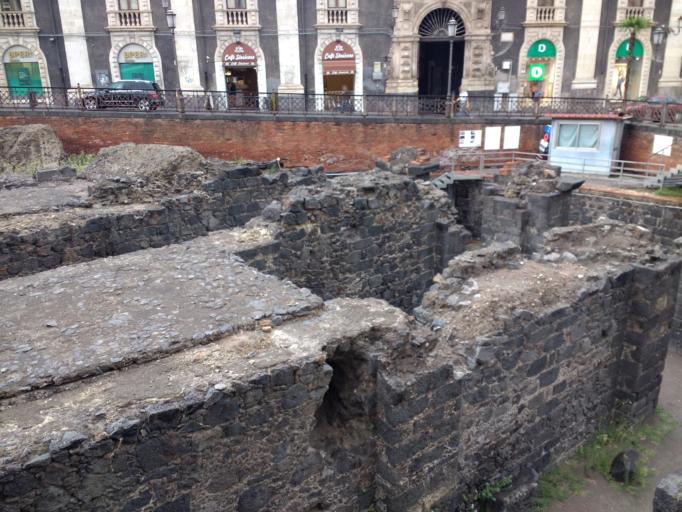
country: IT
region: Sicily
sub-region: Catania
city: Catania
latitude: 37.5072
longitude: 15.0856
